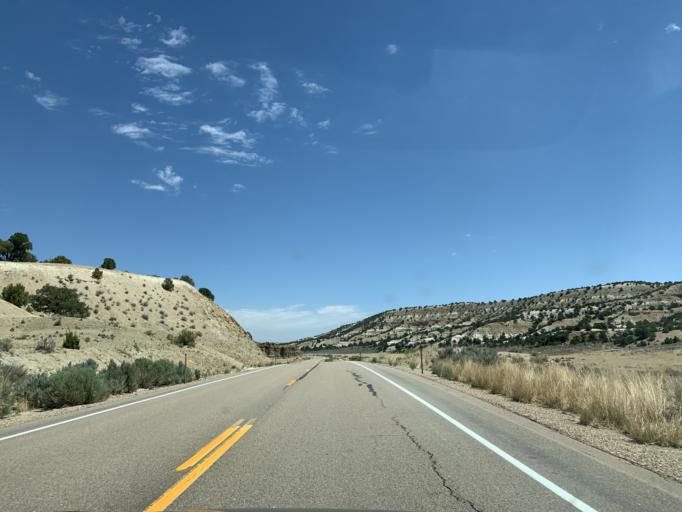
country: US
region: Utah
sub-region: Duchesne County
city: Duchesne
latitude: 39.9512
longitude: -110.1960
